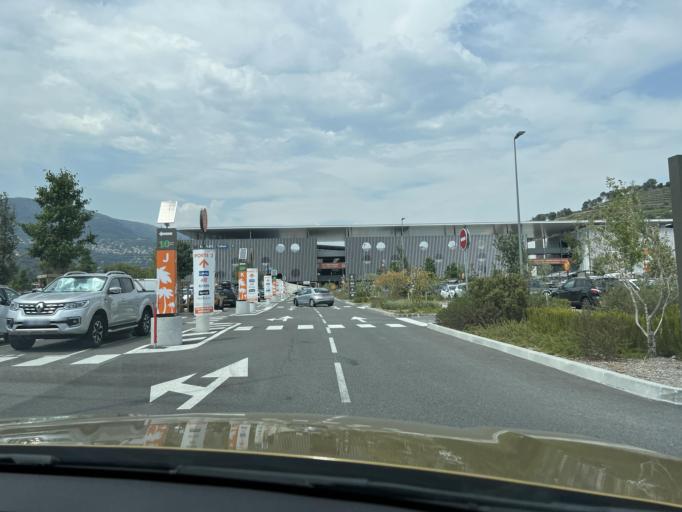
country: FR
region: Provence-Alpes-Cote d'Azur
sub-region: Departement des Alpes-Maritimes
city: Gattieres
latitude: 43.7277
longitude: 7.1870
